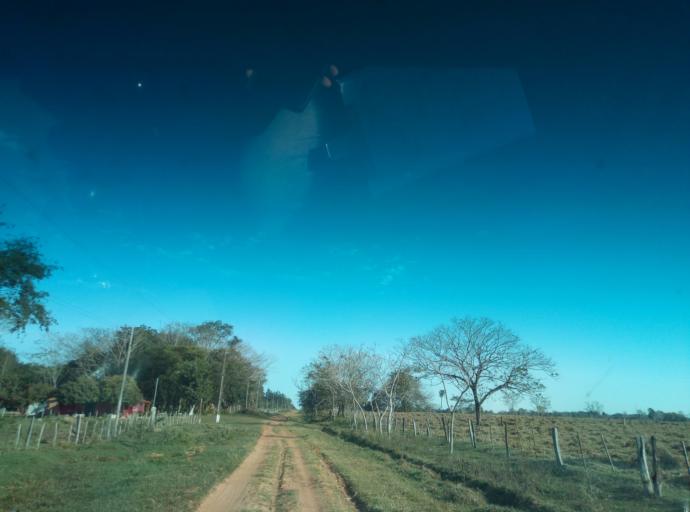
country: PY
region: Caaguazu
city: Doctor Cecilio Baez
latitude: -25.1657
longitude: -56.2321
